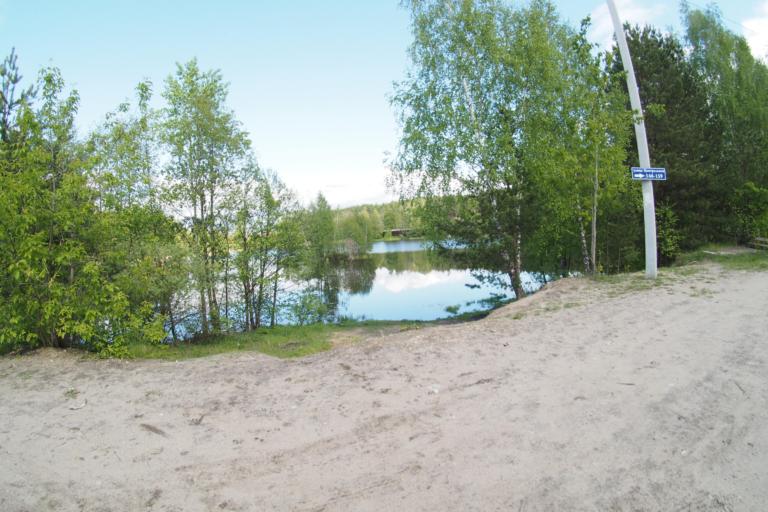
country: RU
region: Moskovskaya
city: Rechitsy
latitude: 55.5426
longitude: 38.4424
